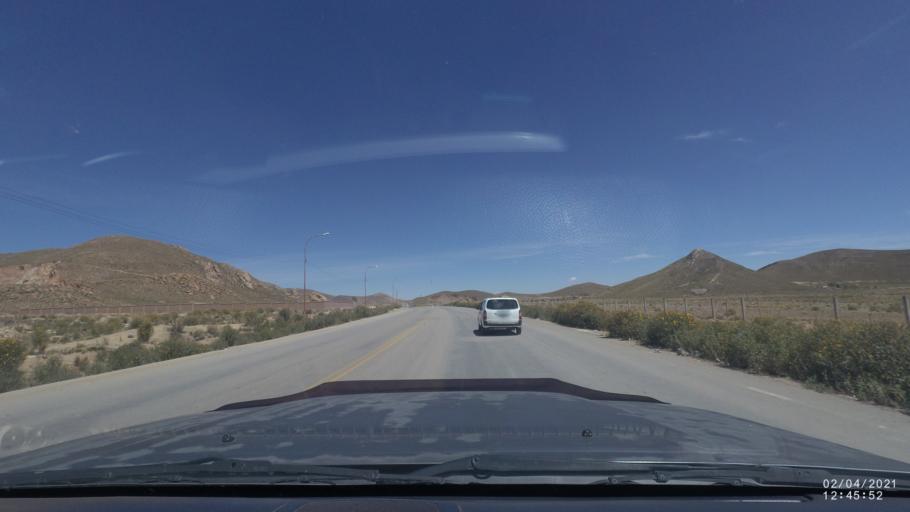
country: BO
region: Oruro
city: Oruro
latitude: -17.9392
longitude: -67.1372
